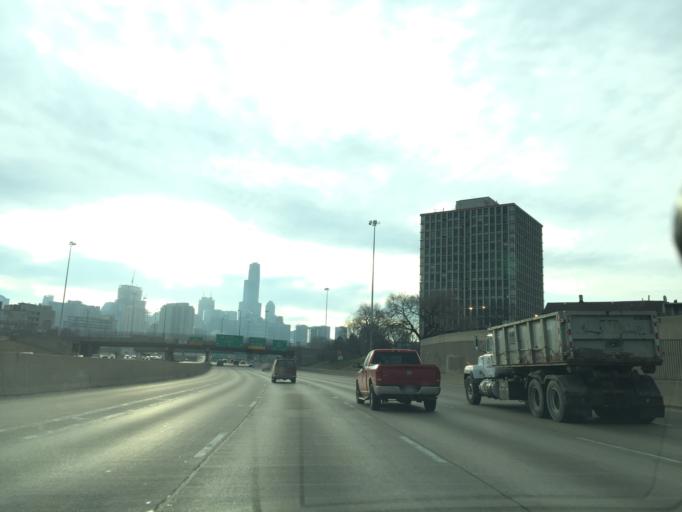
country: US
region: Illinois
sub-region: Cook County
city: Chicago
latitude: 41.8959
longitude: -87.6581
